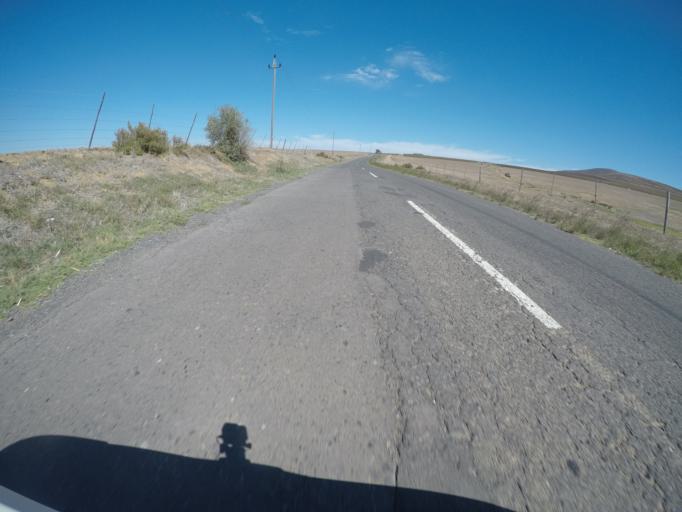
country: ZA
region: Western Cape
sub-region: City of Cape Town
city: Atlantis
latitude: -33.7049
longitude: 18.5862
